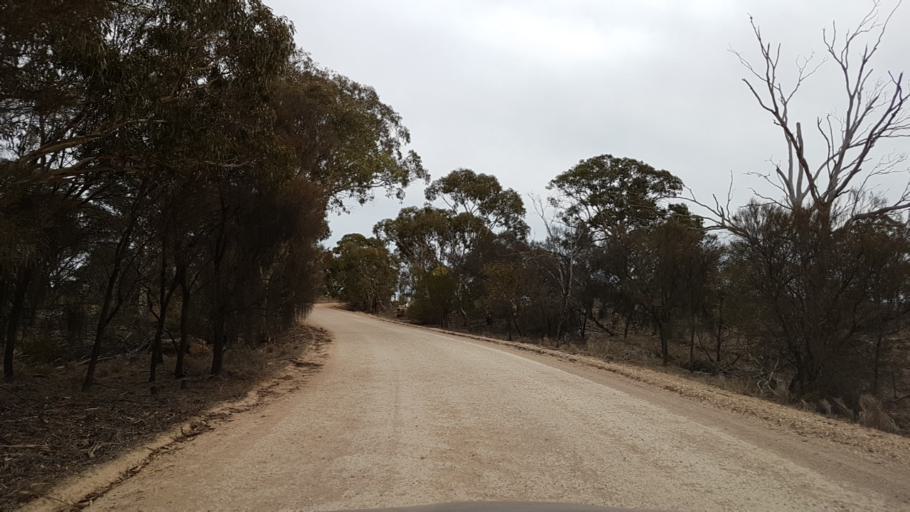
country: AU
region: South Australia
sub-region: Mount Barker
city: Callington
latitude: -35.0052
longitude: 139.0804
